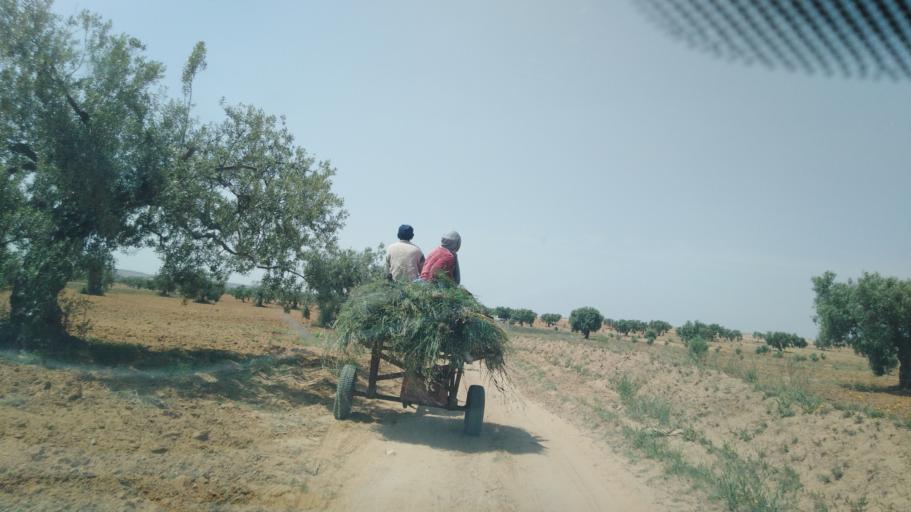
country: TN
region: Safaqis
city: Sfax
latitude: 34.7632
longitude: 10.5789
